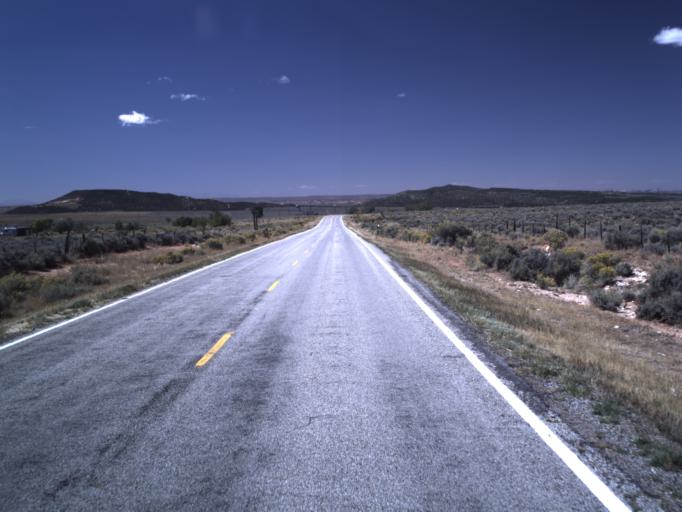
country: US
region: Utah
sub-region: Grand County
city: Moab
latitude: 38.3094
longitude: -109.2877
